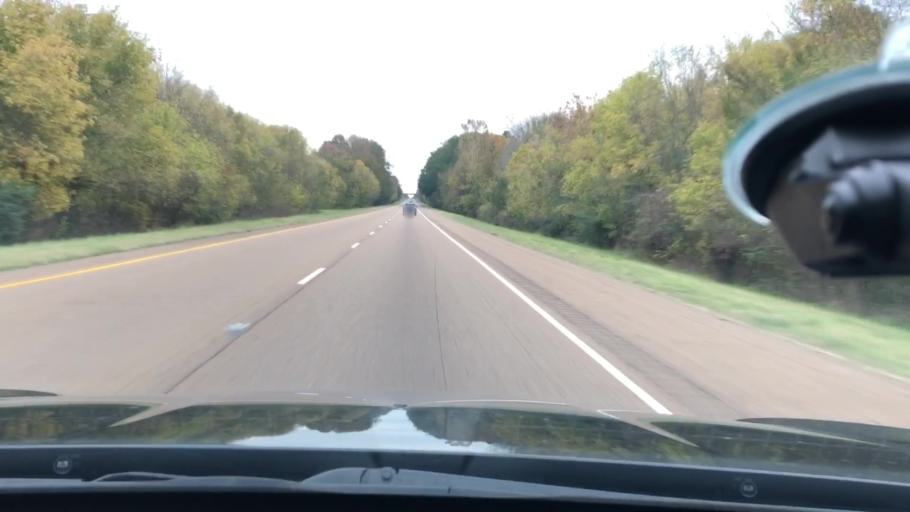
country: US
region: Arkansas
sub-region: Nevada County
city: Prescott
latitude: 33.7596
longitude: -93.4929
